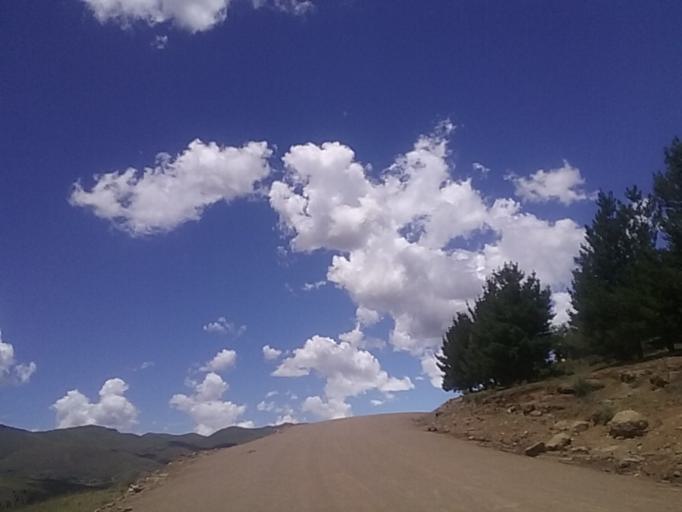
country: LS
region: Qacha's Nek
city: Qacha's Nek
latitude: -30.1687
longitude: 28.2090
